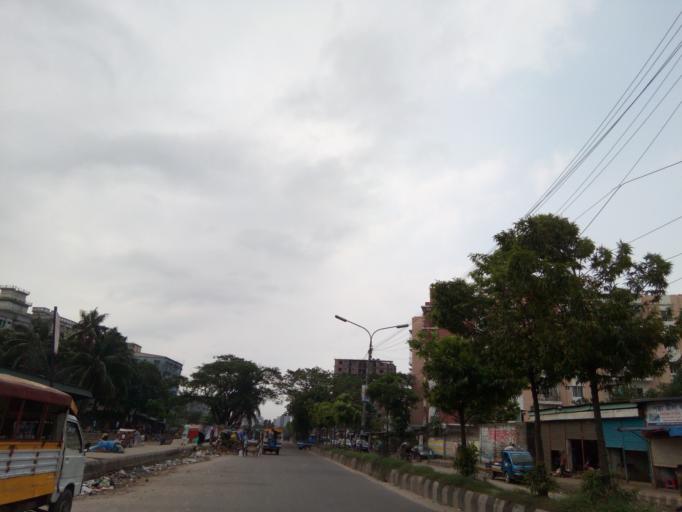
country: BD
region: Dhaka
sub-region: Dhaka
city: Dhaka
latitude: 23.7013
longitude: 90.4294
